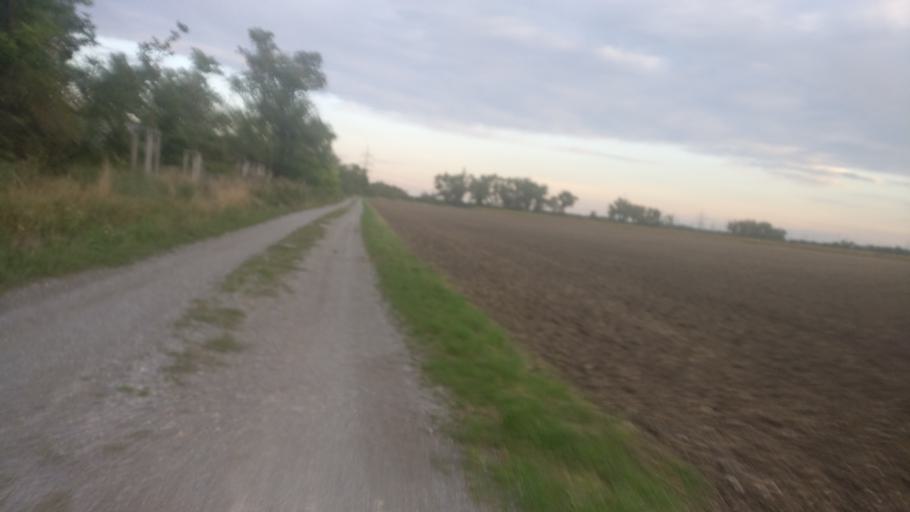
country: AT
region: Lower Austria
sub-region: Politischer Bezirk Modling
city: Munchendorf
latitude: 48.0173
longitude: 16.3774
